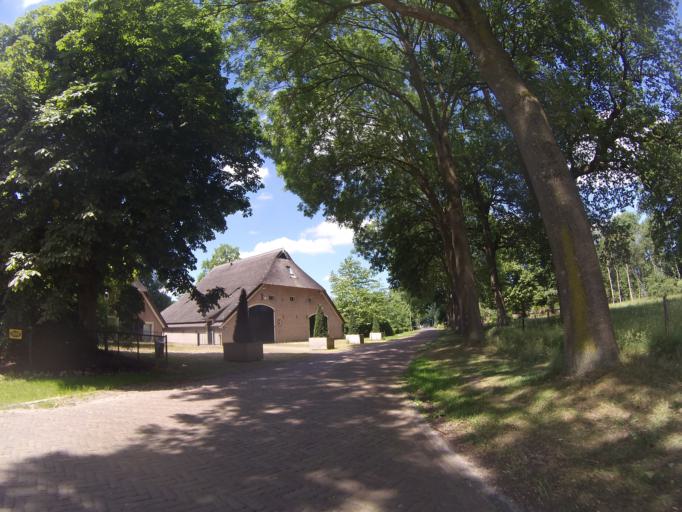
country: NL
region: Drenthe
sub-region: Gemeente Emmen
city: Emmen
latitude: 52.8398
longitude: 6.8819
